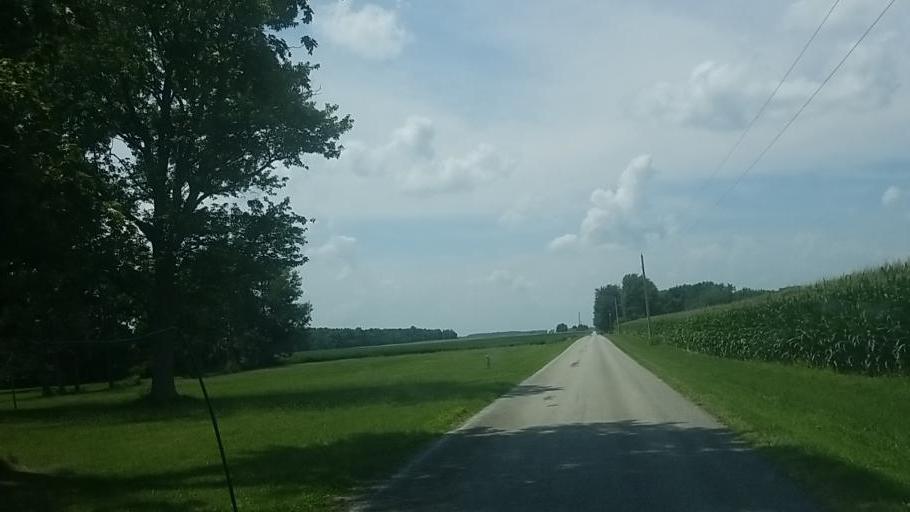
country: US
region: Ohio
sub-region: Marion County
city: Marion
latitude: 40.6733
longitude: -83.2472
